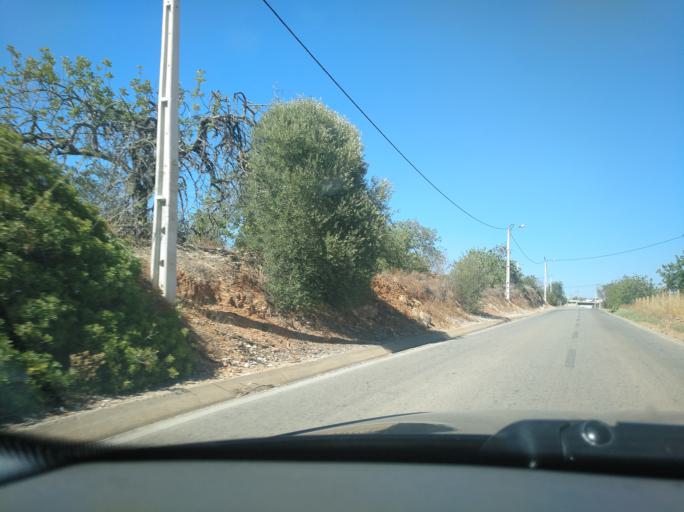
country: PT
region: Faro
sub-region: Faro
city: Faro
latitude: 37.0583
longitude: -7.8997
